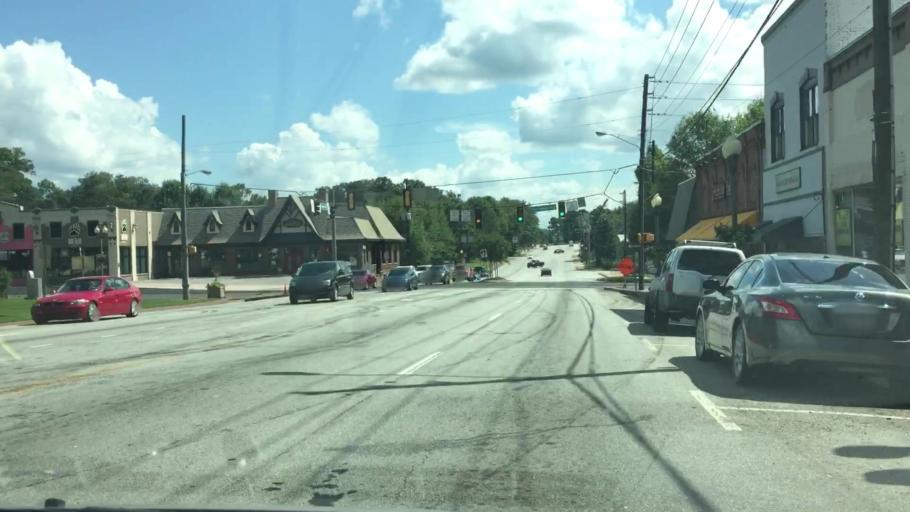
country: US
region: Georgia
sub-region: Fayette County
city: Fayetteville
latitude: 33.4484
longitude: -84.4552
